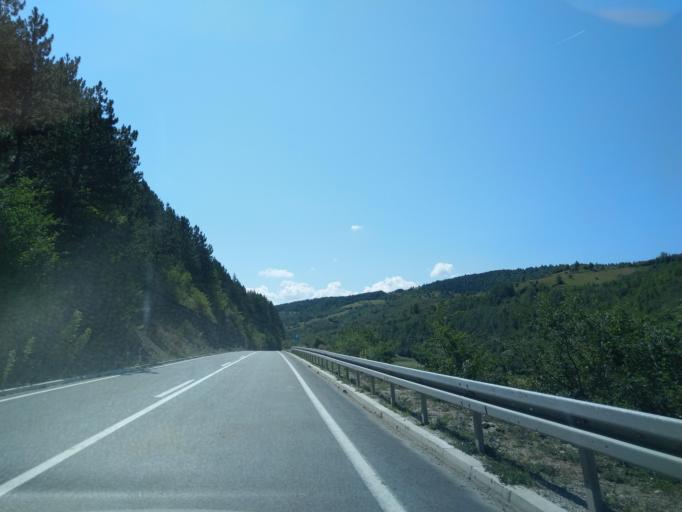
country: RS
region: Central Serbia
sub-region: Zlatiborski Okrug
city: Sjenica
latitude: 43.2915
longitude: 19.9414
